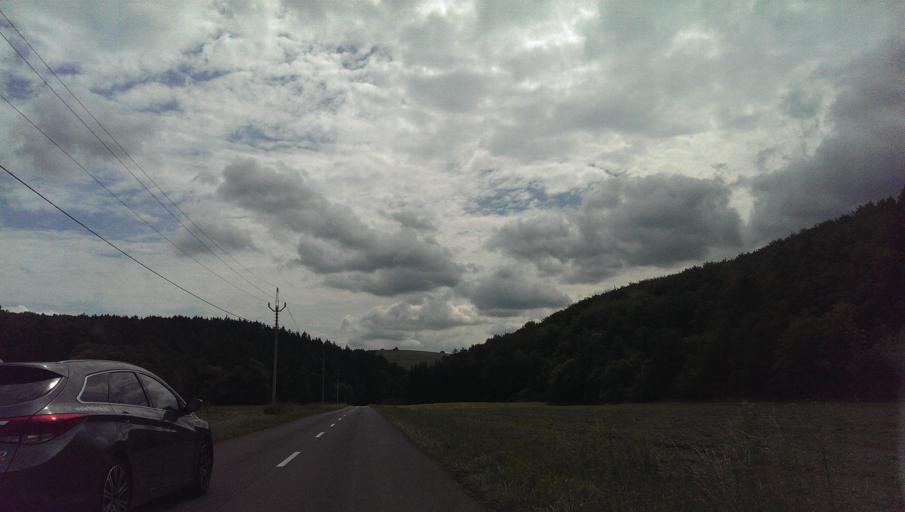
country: CZ
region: South Moravian
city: Velka nad Velickou
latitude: 48.8922
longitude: 17.5761
